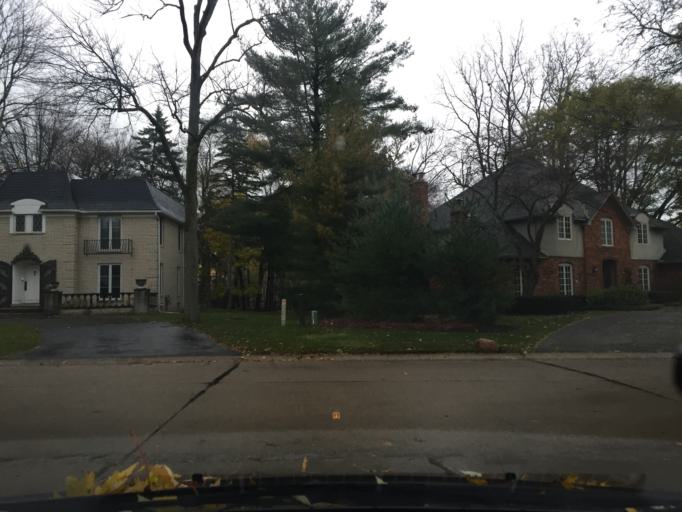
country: US
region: Michigan
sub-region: Oakland County
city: Bloomfield Hills
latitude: 42.5713
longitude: -83.2768
